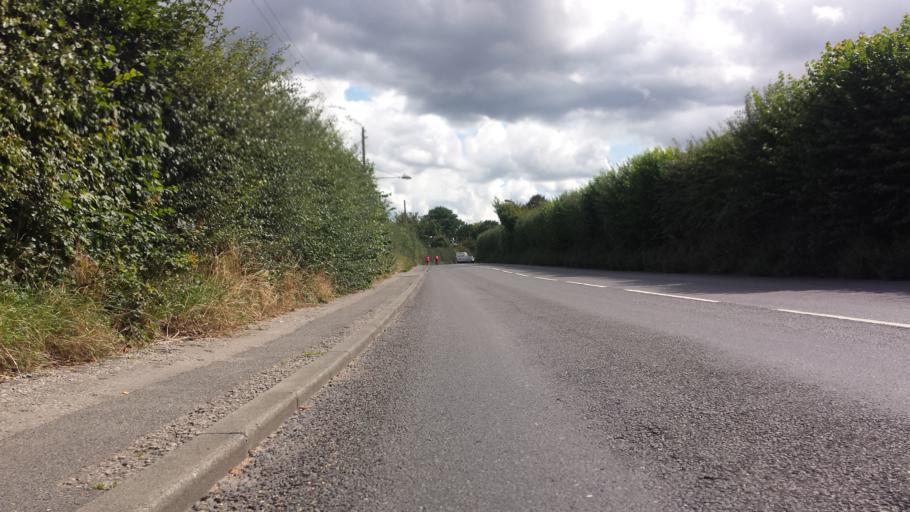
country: GB
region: England
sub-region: Kent
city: Swanley
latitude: 51.4064
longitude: 0.1835
